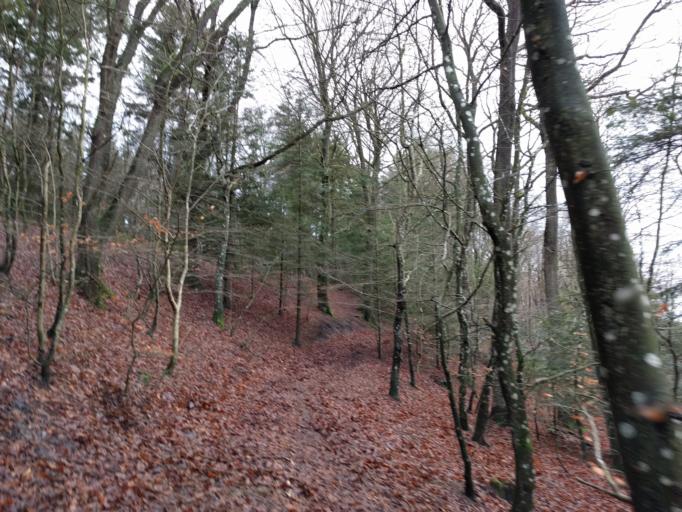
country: DK
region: Central Jutland
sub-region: Silkeborg Kommune
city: Silkeborg
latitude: 56.1668
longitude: 9.5215
